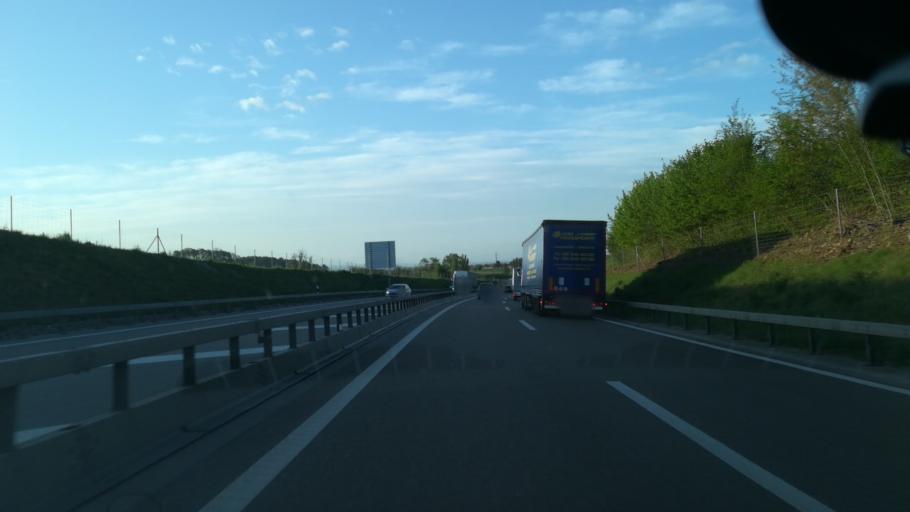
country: CH
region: Zurich
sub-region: Bezirk Andelfingen
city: Dachsen
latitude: 47.6683
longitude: 8.6242
